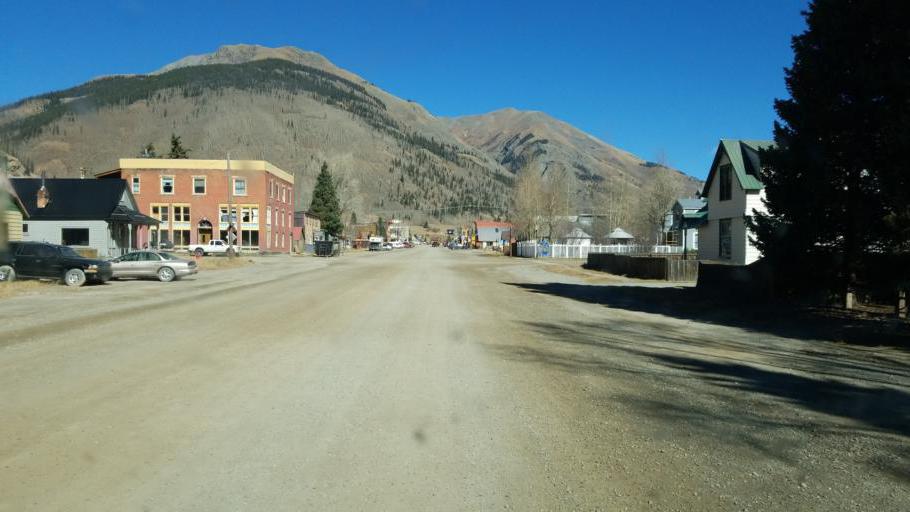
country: US
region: Colorado
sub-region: San Juan County
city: Silverton
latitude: 37.8089
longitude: -107.6654
